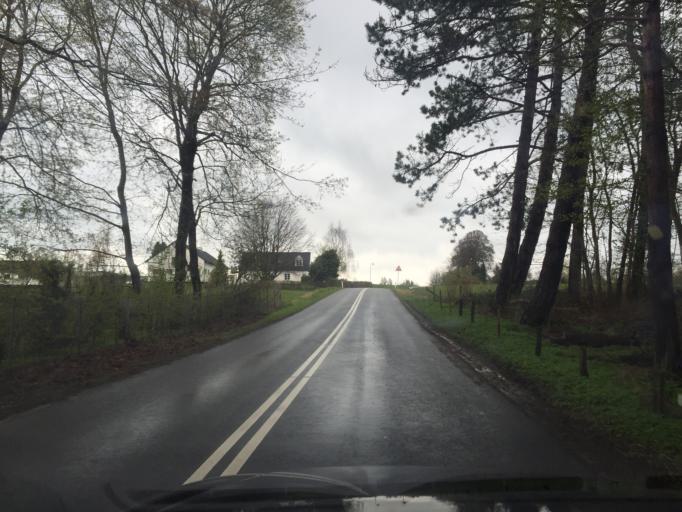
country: DK
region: Capital Region
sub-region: Egedal Kommune
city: Smorumnedre
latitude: 55.7050
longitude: 12.2624
